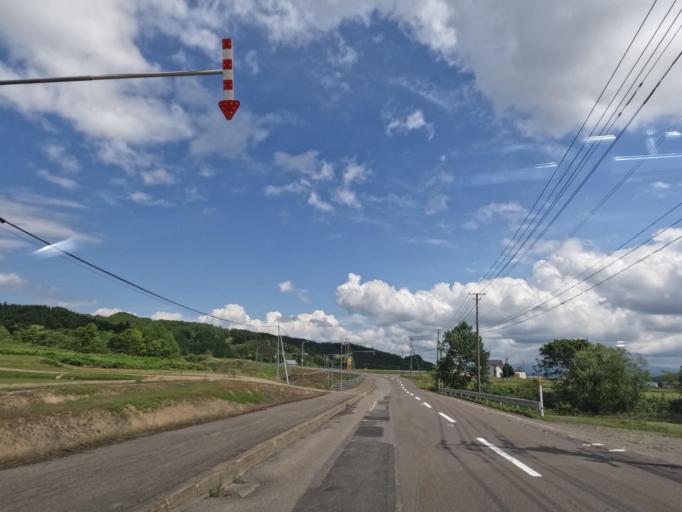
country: JP
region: Hokkaido
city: Takikawa
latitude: 43.5809
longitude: 141.8207
